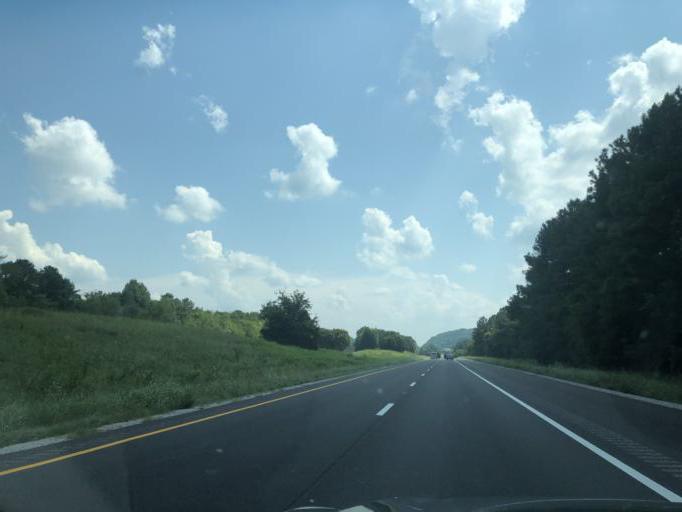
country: US
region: Tennessee
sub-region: Rutherford County
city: Plainview
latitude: 35.6138
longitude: -86.2408
